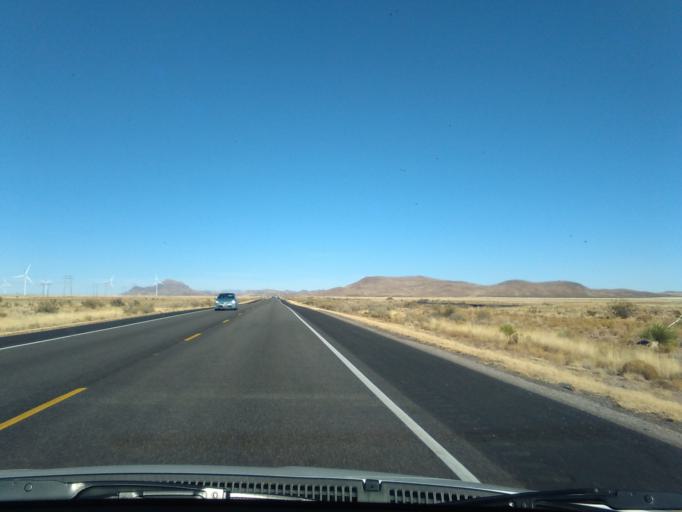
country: US
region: New Mexico
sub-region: Luna County
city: Deming
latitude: 32.5034
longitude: -107.5104
